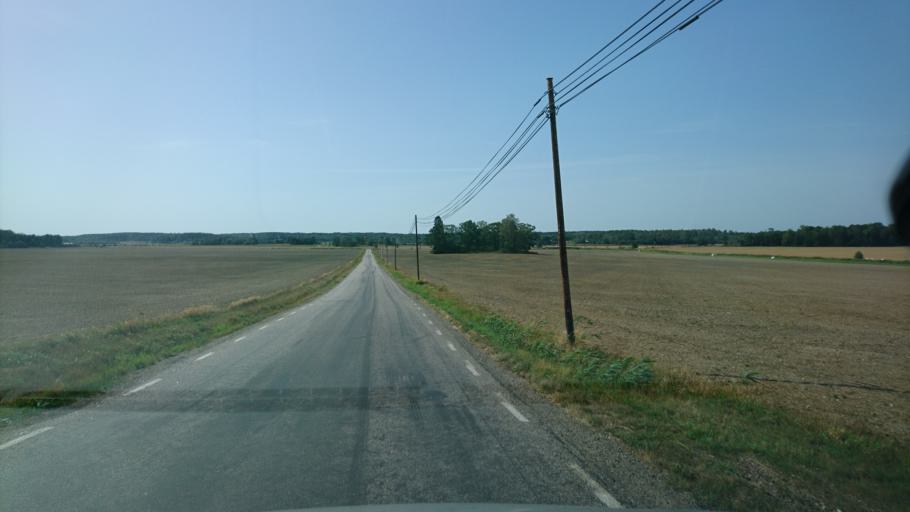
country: SE
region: Soedermanland
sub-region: Strangnas Kommun
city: Strangnas
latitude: 59.3503
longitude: 17.0709
